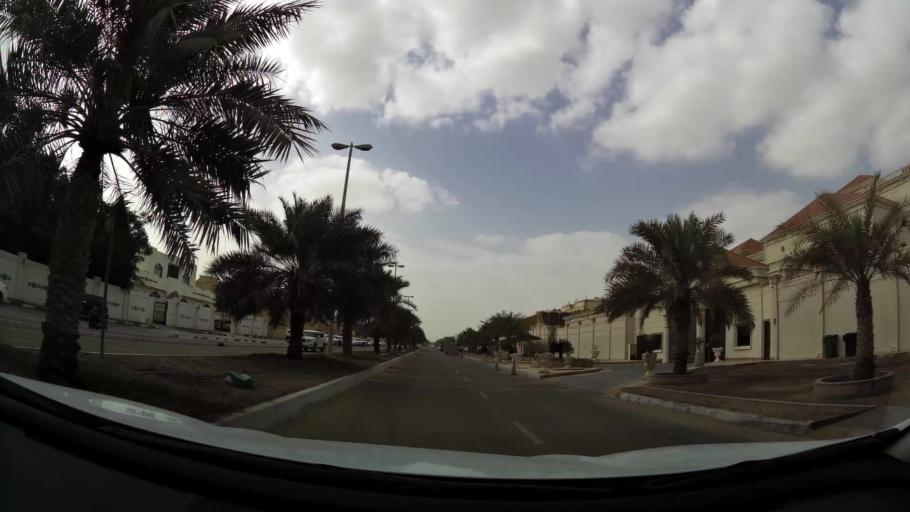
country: AE
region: Abu Dhabi
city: Abu Dhabi
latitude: 24.4092
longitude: 54.4962
